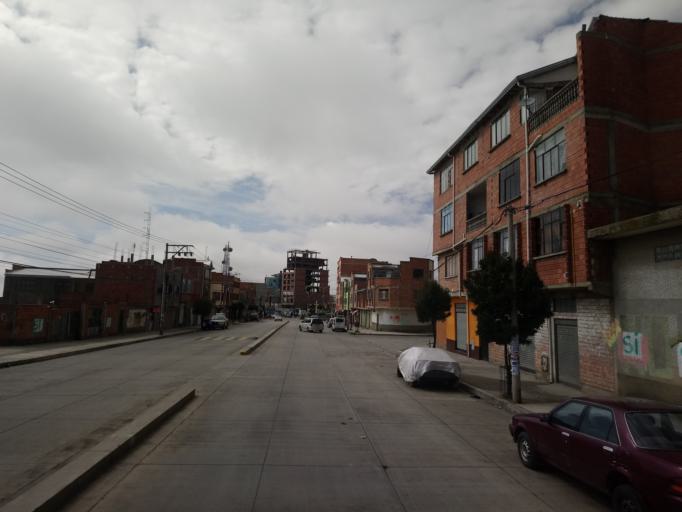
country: BO
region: La Paz
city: La Paz
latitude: -16.5164
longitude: -68.1511
